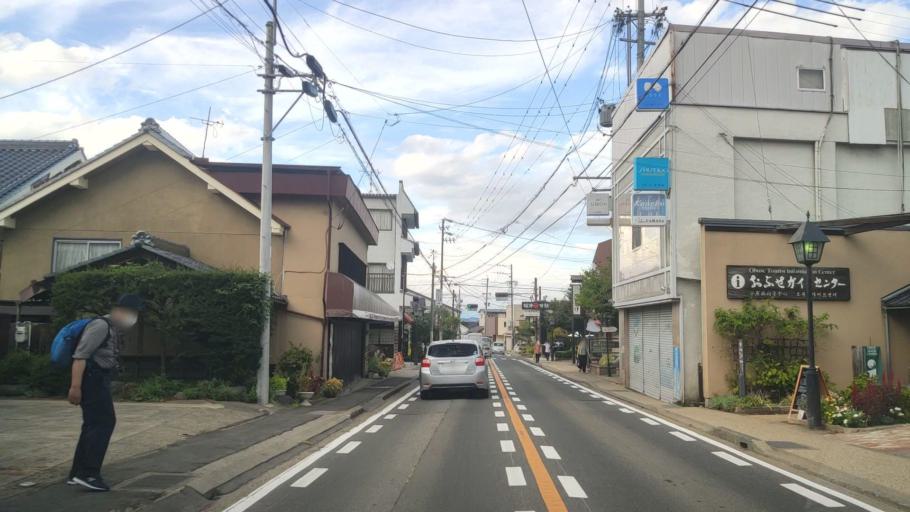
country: JP
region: Nagano
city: Suzaka
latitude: 36.6962
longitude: 138.3162
